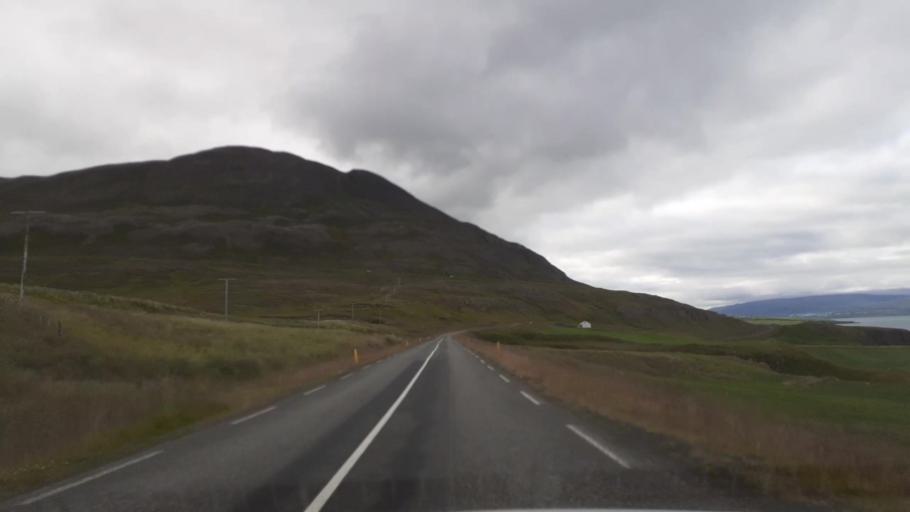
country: IS
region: Northeast
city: Akureyri
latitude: 65.8200
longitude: -18.0501
